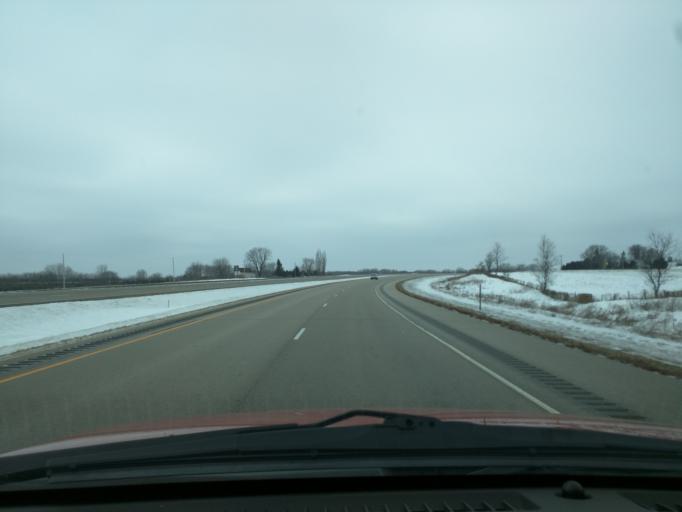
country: US
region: Wisconsin
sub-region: Trempealeau County
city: Trempealeau
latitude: 43.9135
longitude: -91.5161
